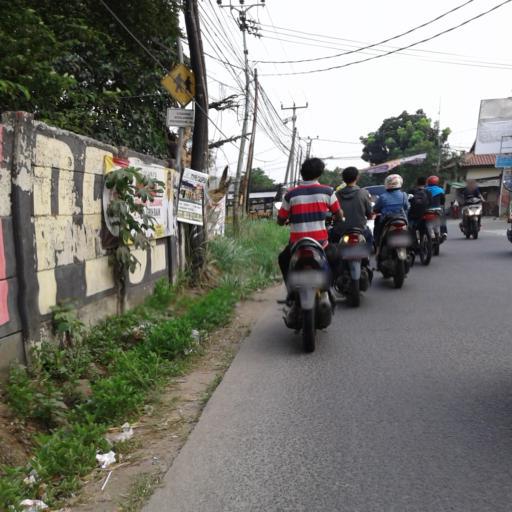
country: ID
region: West Java
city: Sawangan
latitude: -6.3882
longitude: 106.7688
